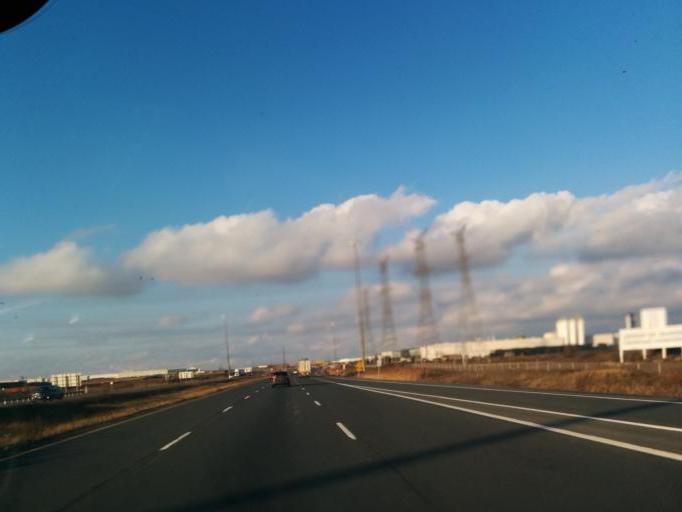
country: CA
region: Ontario
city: Etobicoke
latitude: 43.7591
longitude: -79.6324
